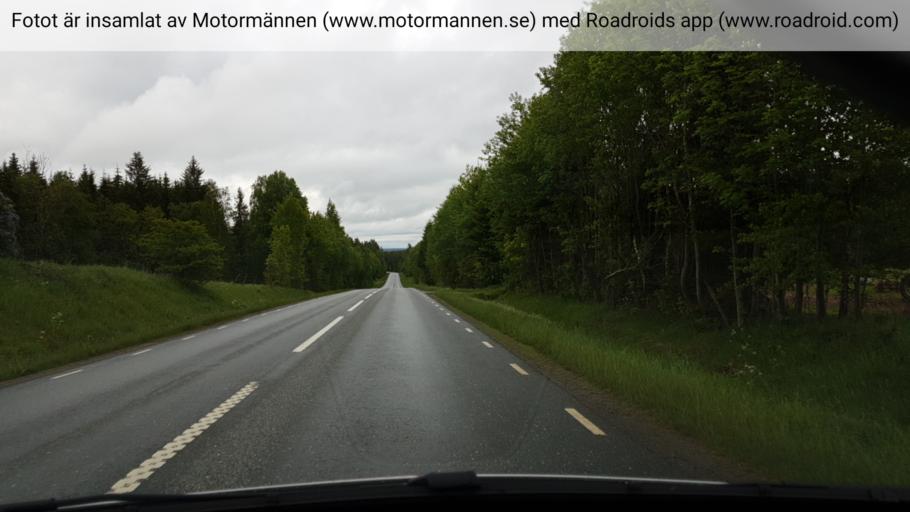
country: SE
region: Joenkoeping
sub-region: Aneby Kommun
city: Aneby
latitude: 57.8047
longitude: 14.7131
